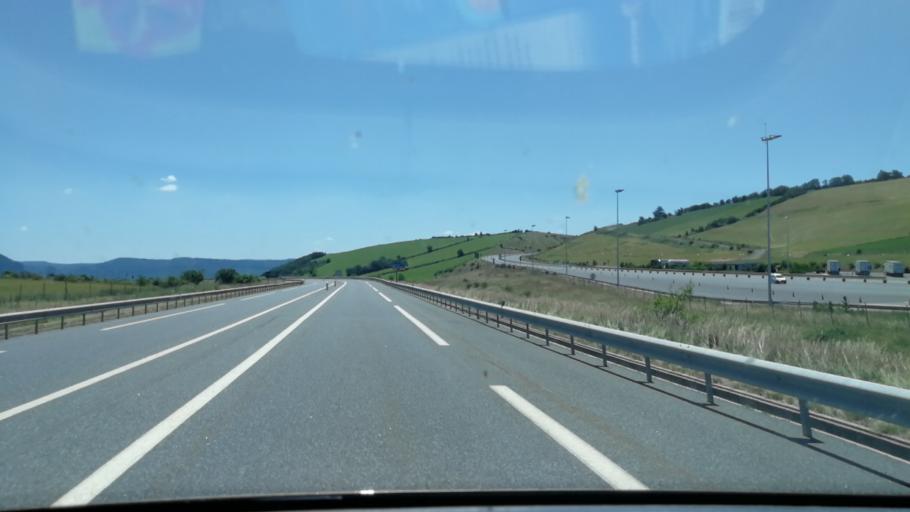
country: FR
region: Midi-Pyrenees
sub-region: Departement de l'Aveyron
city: Creissels
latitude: 44.1352
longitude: 3.0261
